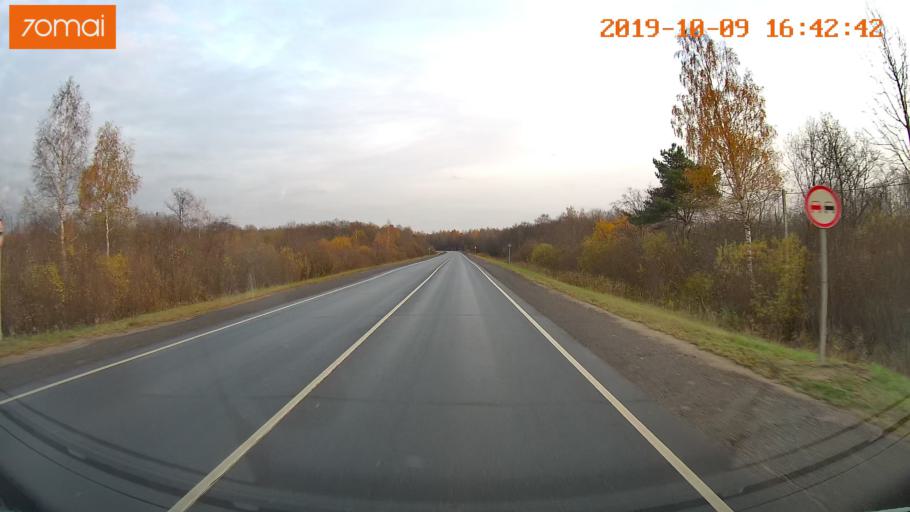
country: RU
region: Kostroma
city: Volgorechensk
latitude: 57.4594
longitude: 41.1056
